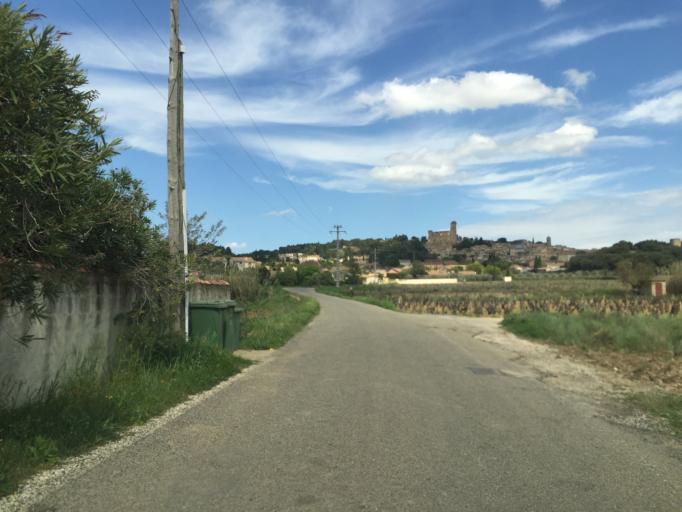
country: FR
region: Provence-Alpes-Cote d'Azur
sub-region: Departement du Vaucluse
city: Chateauneuf-du-Pape
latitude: 44.0509
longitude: 4.8257
